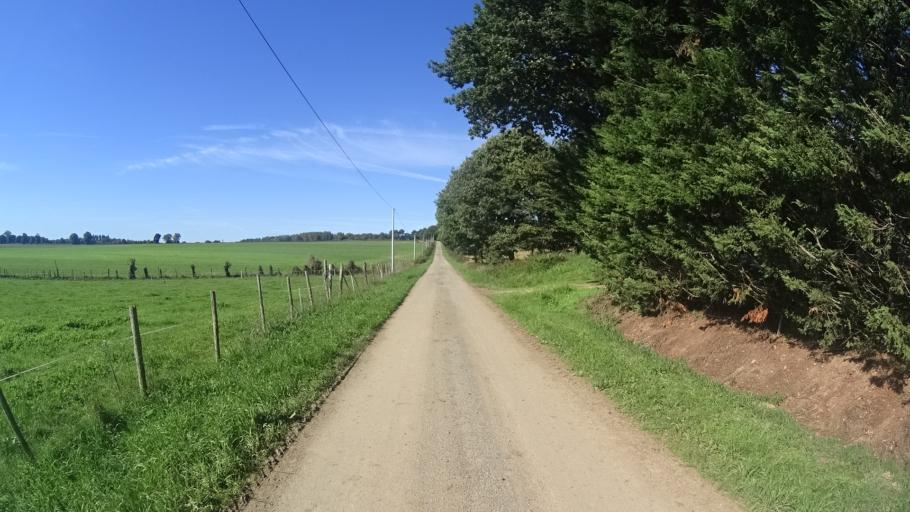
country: FR
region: Brittany
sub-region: Departement du Morbihan
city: La Gacilly
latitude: 47.7436
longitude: -2.1662
